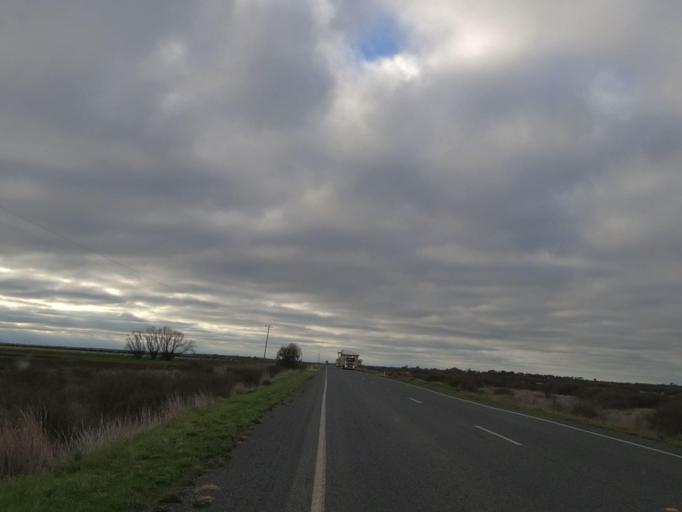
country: AU
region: Victoria
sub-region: Swan Hill
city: Swan Hill
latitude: -35.8541
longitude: 143.9364
